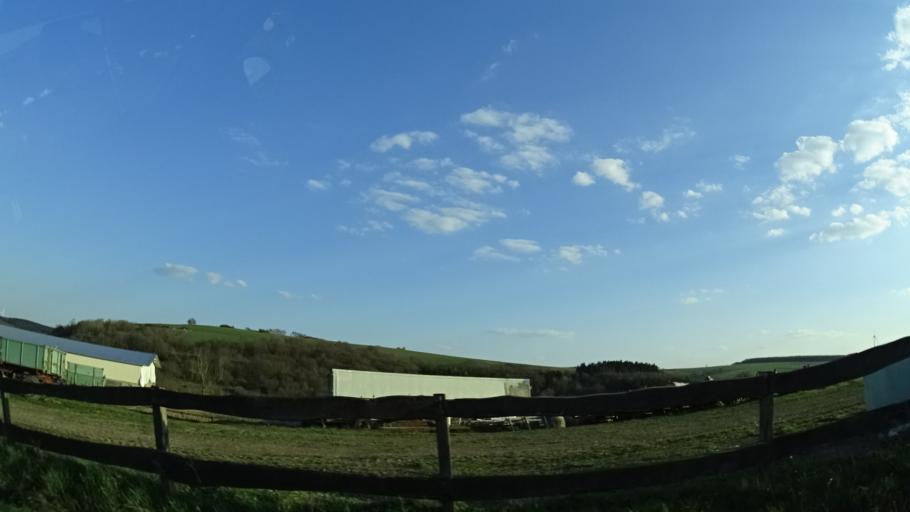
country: DE
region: Rheinland-Pfalz
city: Obermoschel
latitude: 49.7250
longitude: 7.7603
